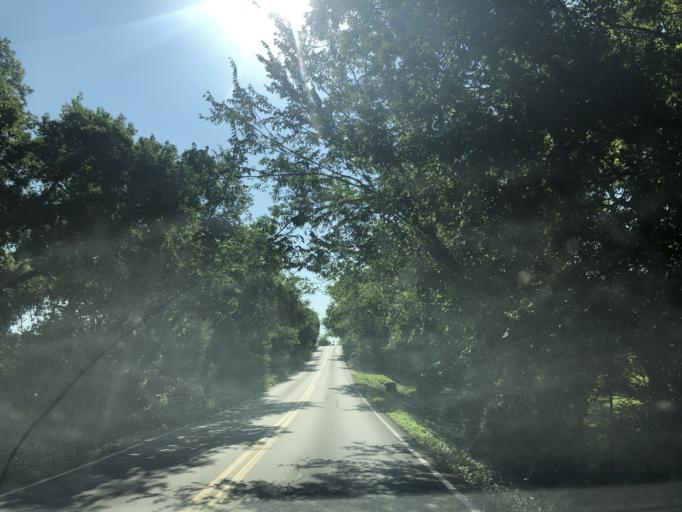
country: US
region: Texas
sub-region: Dallas County
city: Sunnyvale
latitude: 32.8229
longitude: -96.5899
